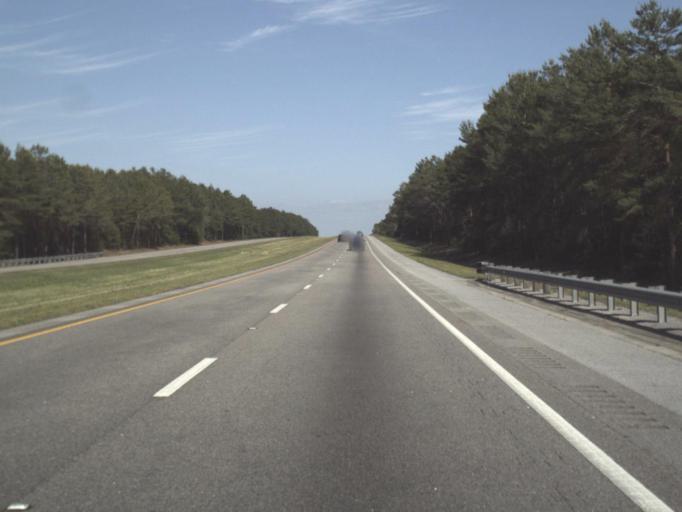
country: US
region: Florida
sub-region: Okaloosa County
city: Crestview
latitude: 30.7193
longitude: -86.4651
